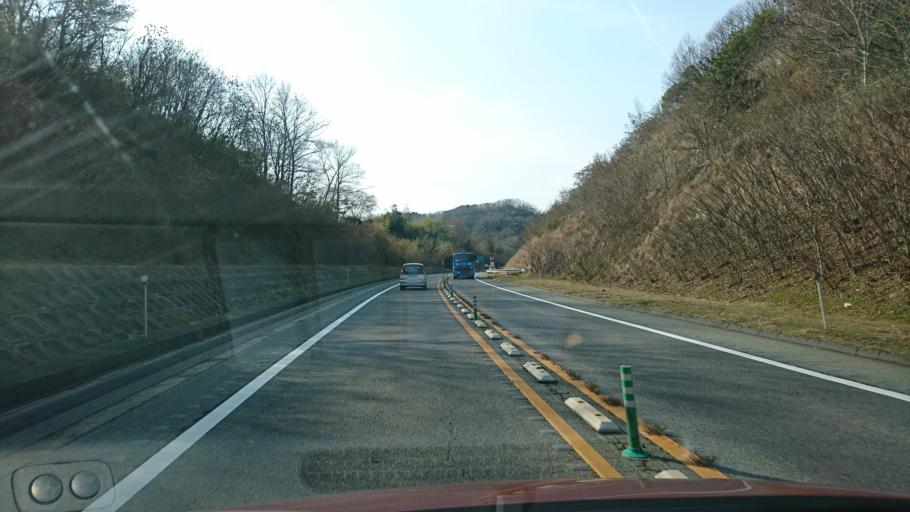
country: JP
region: Hiroshima
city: Onomichi
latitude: 34.3885
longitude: 133.2047
